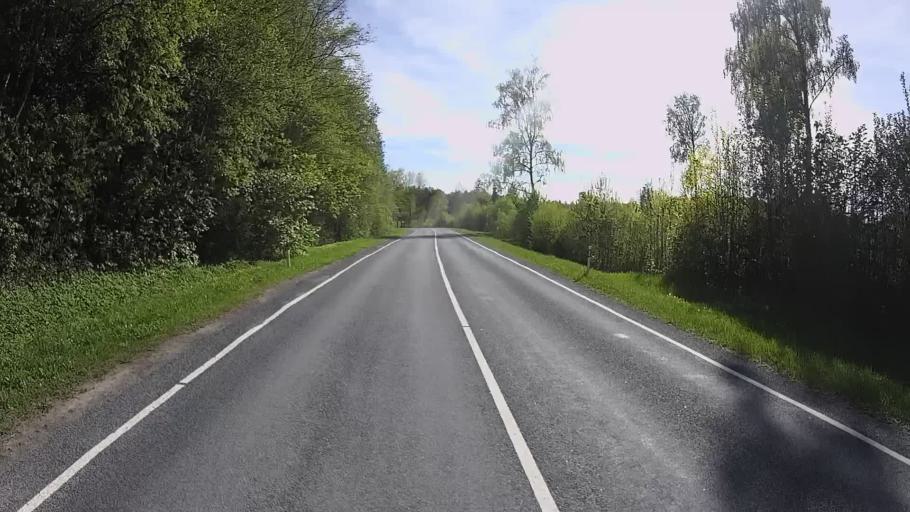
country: EE
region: Vorumaa
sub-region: Antsla vald
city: Vana-Antsla
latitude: 57.9720
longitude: 26.4638
